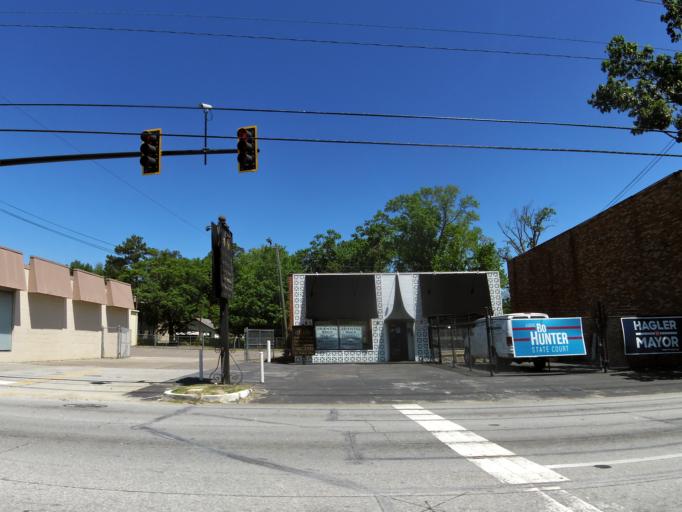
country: US
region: Georgia
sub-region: Richmond County
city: Augusta
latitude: 33.4758
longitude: -82.0020
